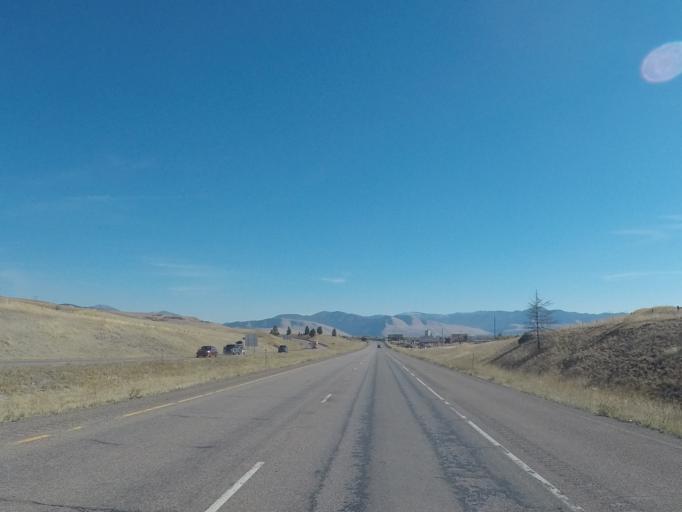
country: US
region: Montana
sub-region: Missoula County
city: Orchard Homes
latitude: 46.9430
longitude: -114.1169
